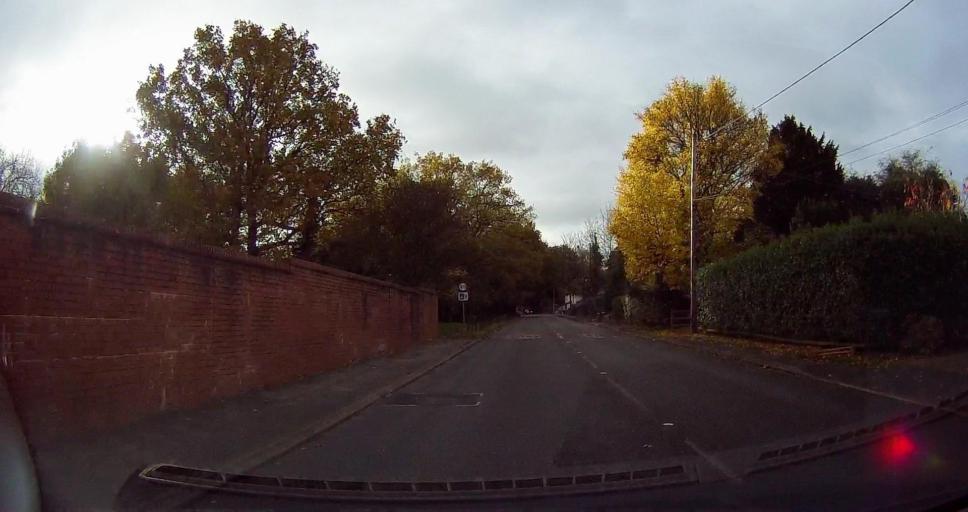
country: GB
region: England
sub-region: Kent
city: Meopham
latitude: 51.3406
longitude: 0.3454
